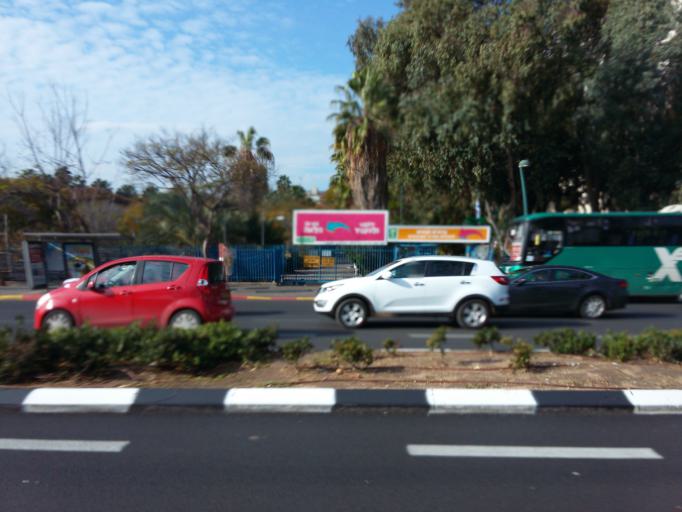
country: IL
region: Tel Aviv
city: Tel Aviv
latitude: 32.1001
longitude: 34.7924
